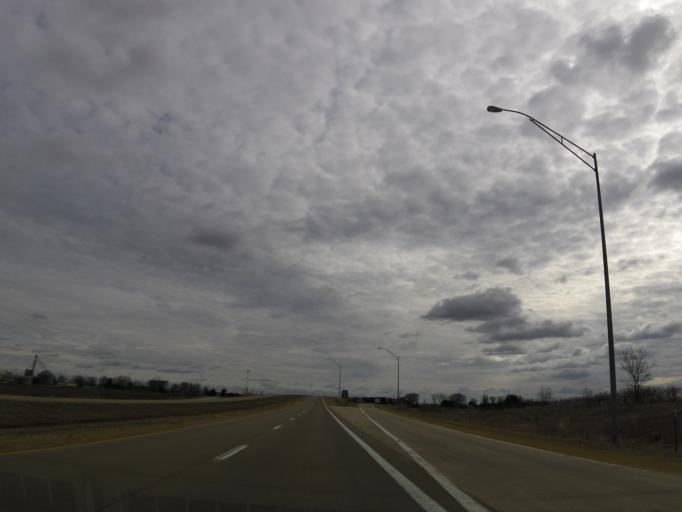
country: US
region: Iowa
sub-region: Chickasaw County
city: New Hampton
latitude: 43.0726
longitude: -92.3334
